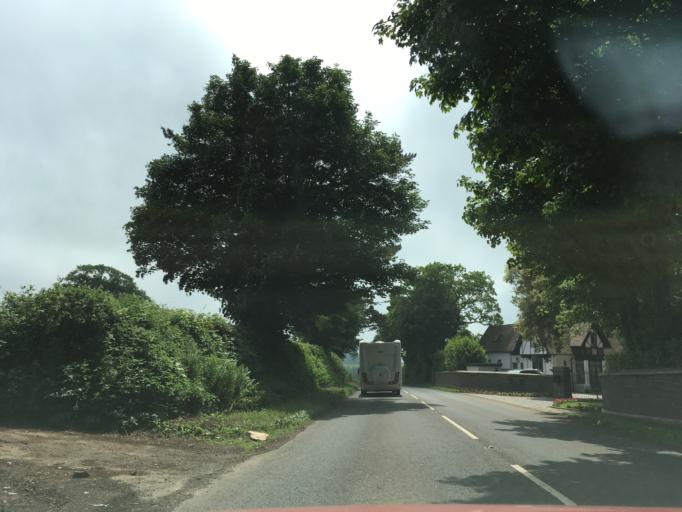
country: GB
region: England
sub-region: Devon
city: Totnes
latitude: 50.4162
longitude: -3.7061
